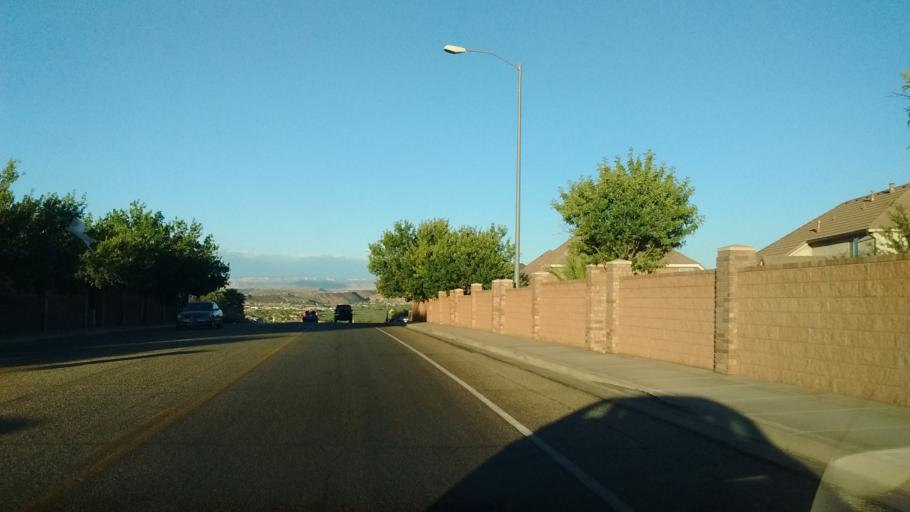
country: US
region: Utah
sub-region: Washington County
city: Saint George
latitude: 37.0935
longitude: -113.5463
